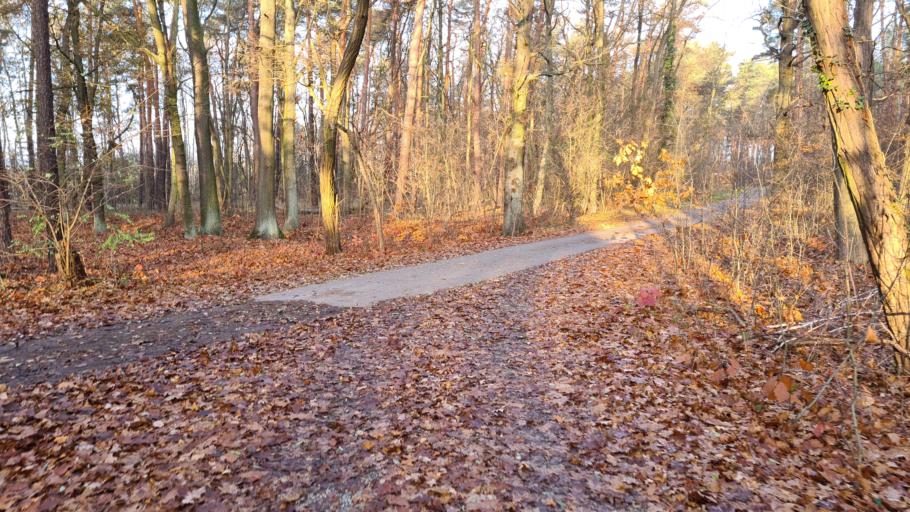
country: DE
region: Brandenburg
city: Calau
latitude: 51.7294
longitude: 13.9818
